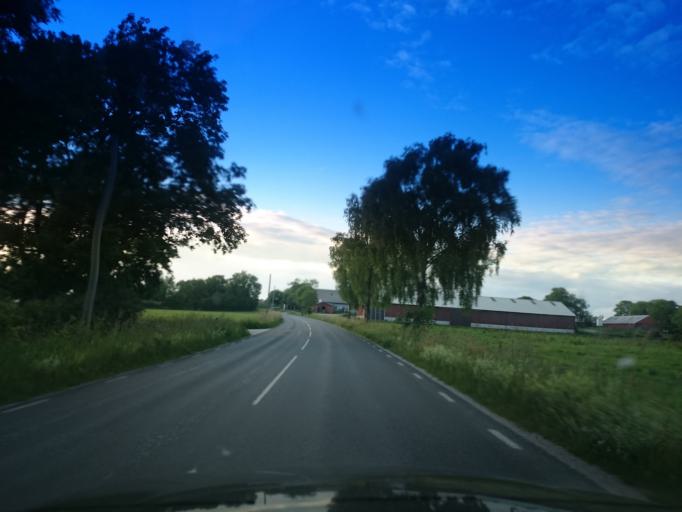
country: SE
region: Gotland
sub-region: Gotland
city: Hemse
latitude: 57.3188
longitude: 18.3854
